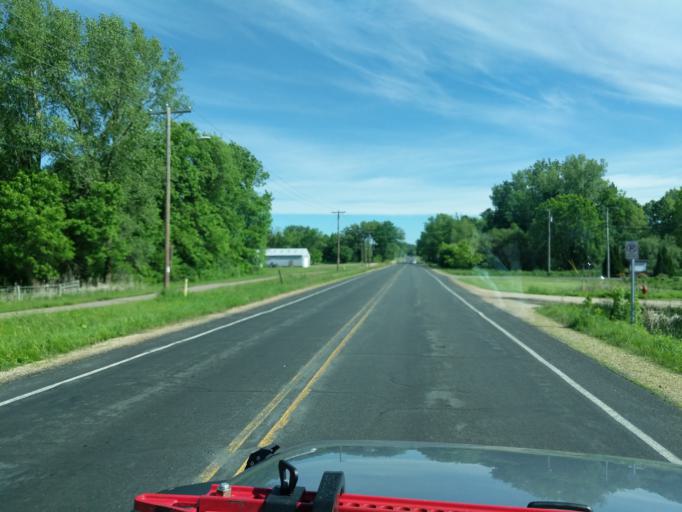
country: US
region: Wisconsin
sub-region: Pierce County
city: River Falls
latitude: 44.8448
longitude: -92.6089
